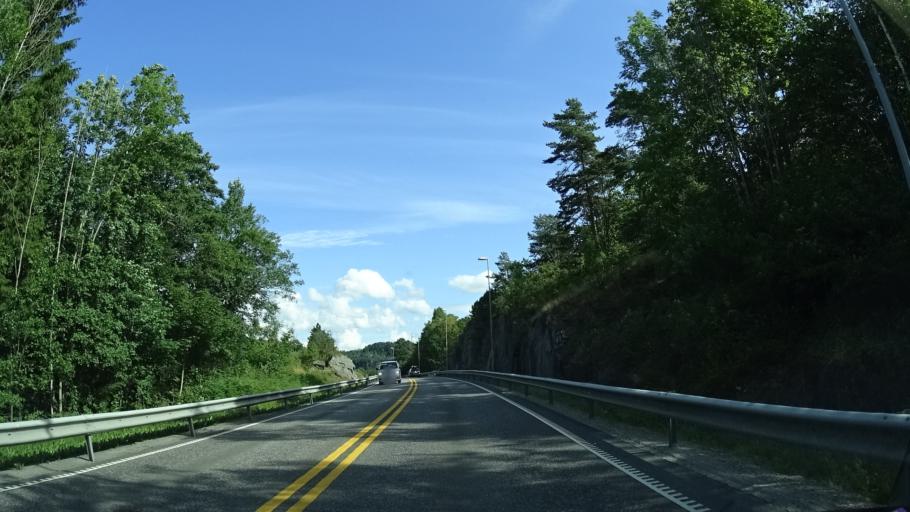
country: NO
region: Telemark
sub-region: Bamble
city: Langesund
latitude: 59.0255
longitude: 9.6796
